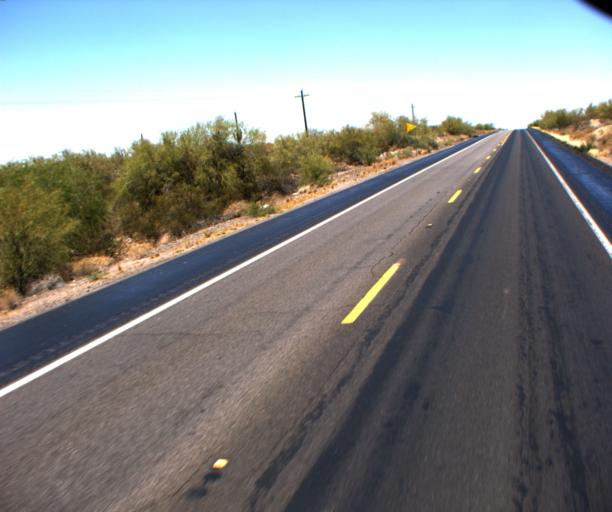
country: US
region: Arizona
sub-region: Pinal County
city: Florence
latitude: 33.0878
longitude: -111.3737
